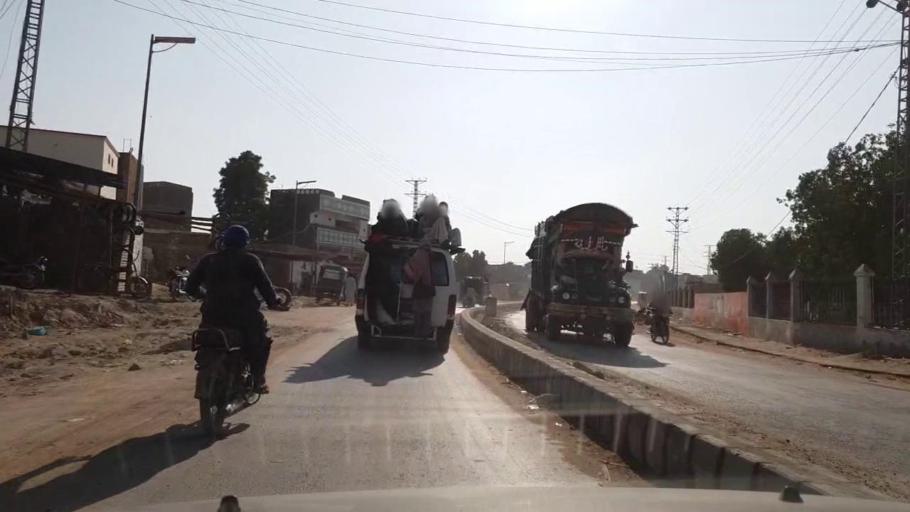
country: PK
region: Sindh
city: Tando Muhammad Khan
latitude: 25.1217
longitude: 68.5433
